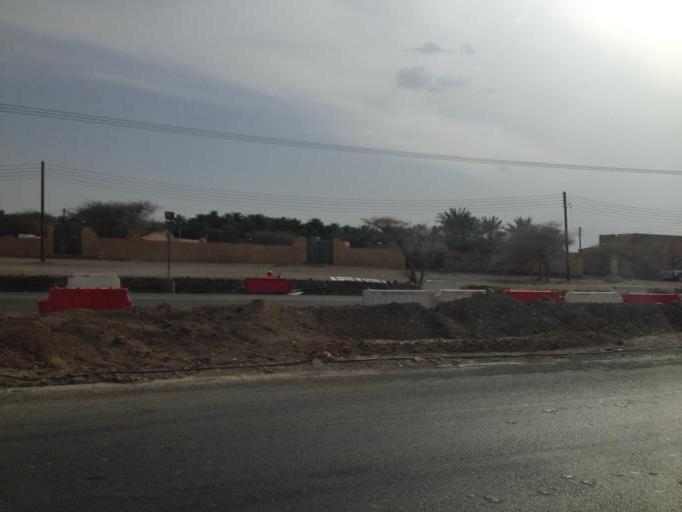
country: OM
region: Ash Sharqiyah
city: Al Qabil
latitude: 22.5694
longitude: 58.6993
